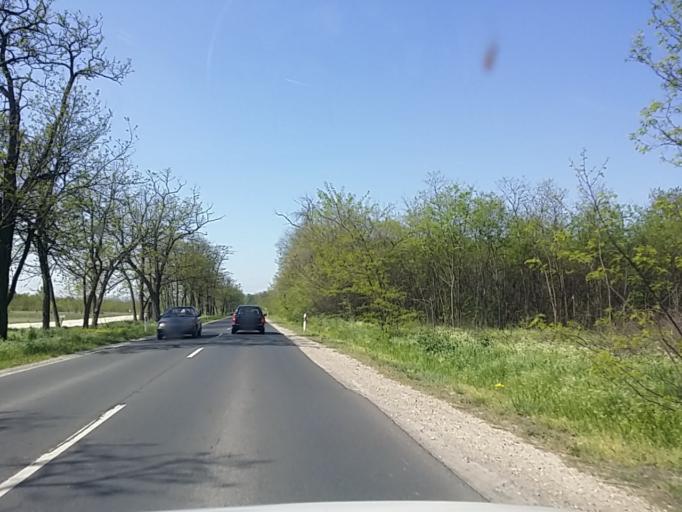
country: HU
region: Pest
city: Fot
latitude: 47.6001
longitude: 19.1868
